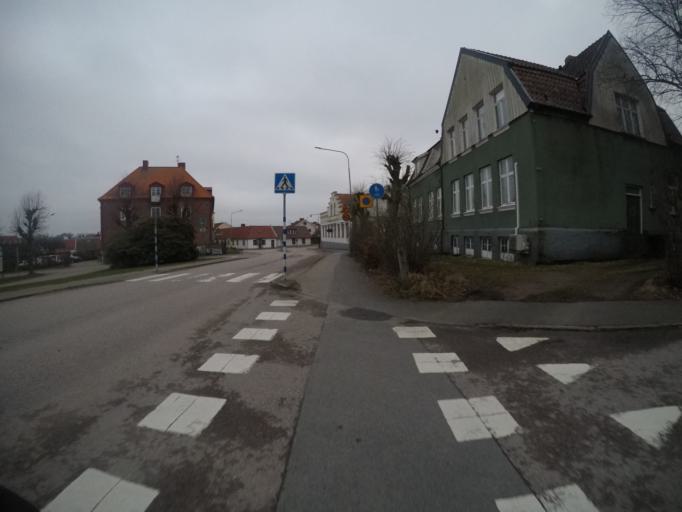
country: SE
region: Halland
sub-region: Laholms Kommun
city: Laholm
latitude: 56.5104
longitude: 13.0410
